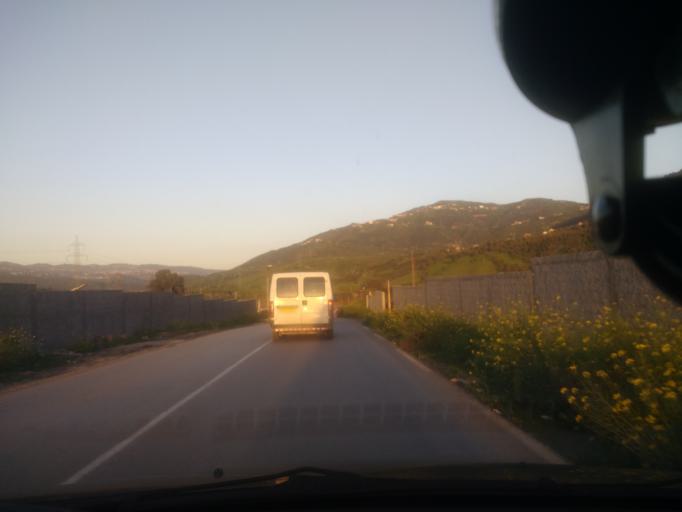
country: DZ
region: Boumerdes
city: Makouda
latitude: 36.7597
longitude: 4.0628
